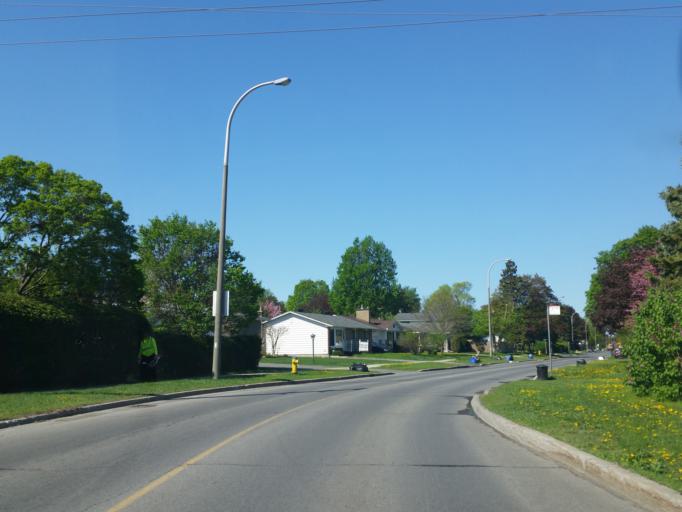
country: CA
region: Ontario
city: Ottawa
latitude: 45.3417
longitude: -75.7353
